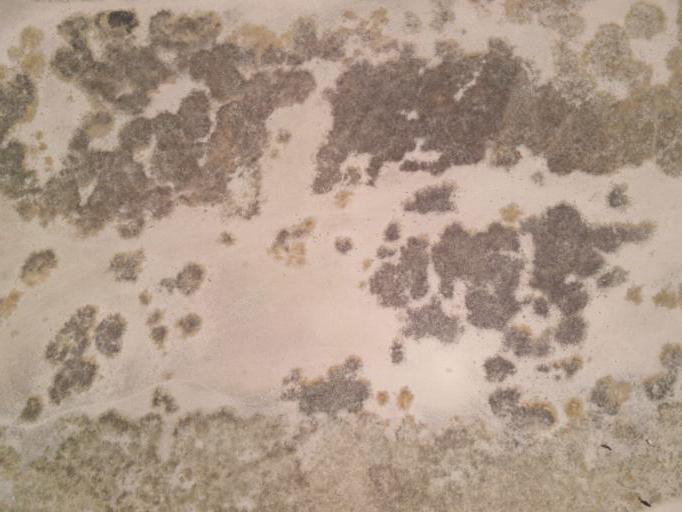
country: BO
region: La Paz
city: Batallas
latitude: -16.3544
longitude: -68.6295
